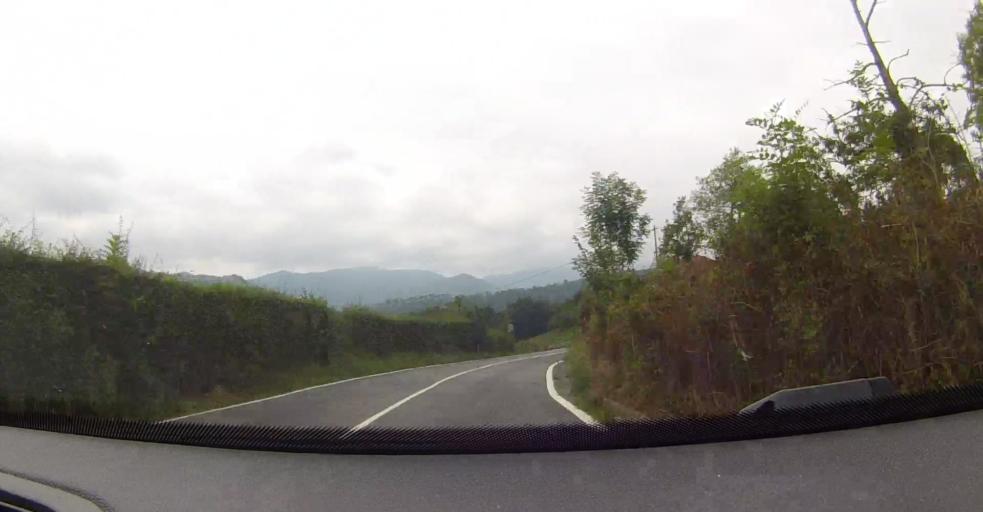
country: ES
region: Basque Country
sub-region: Bizkaia
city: Lanestosa
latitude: 43.2370
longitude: -3.3262
